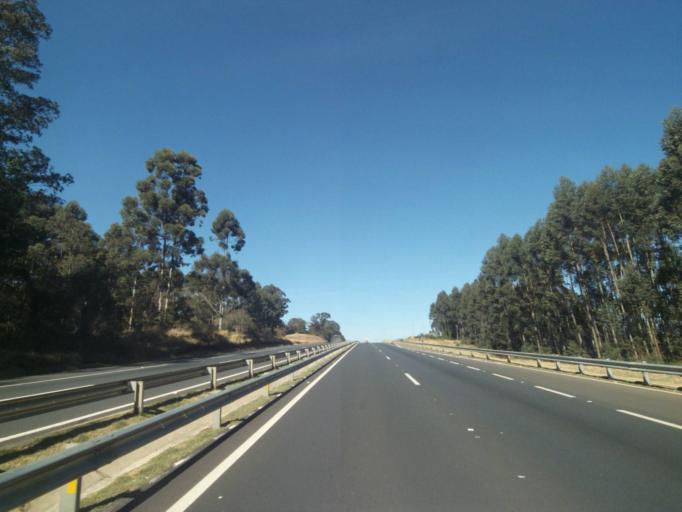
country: BR
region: Parana
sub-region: Tibagi
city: Tibagi
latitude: -24.8418
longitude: -50.4753
